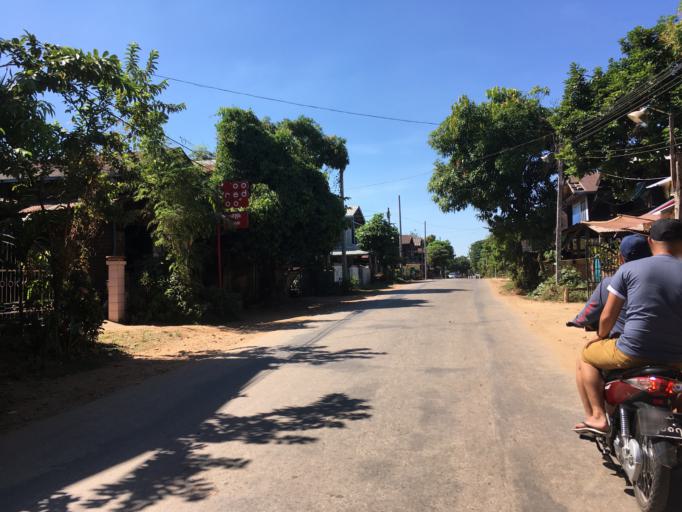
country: MM
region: Mon
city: Kyaikkami
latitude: 15.5093
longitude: 97.8519
